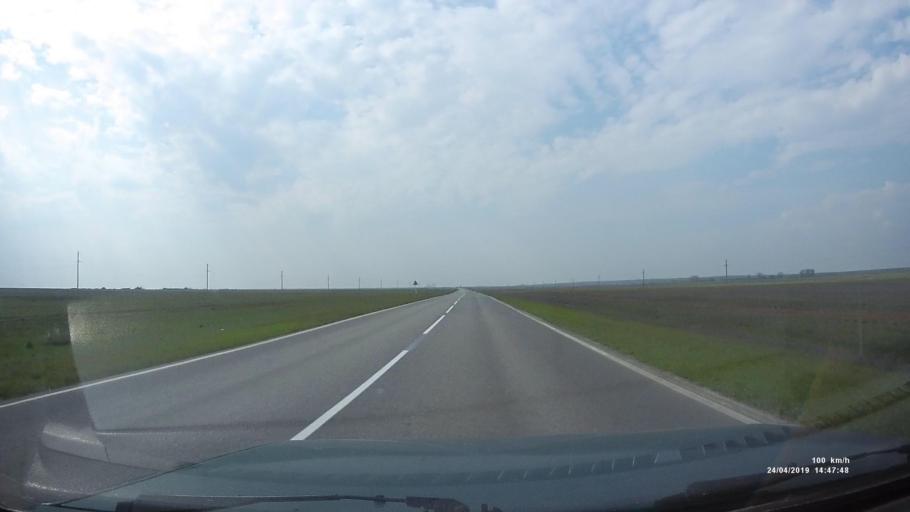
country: RU
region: Rostov
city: Remontnoye
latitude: 46.4950
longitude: 43.7667
